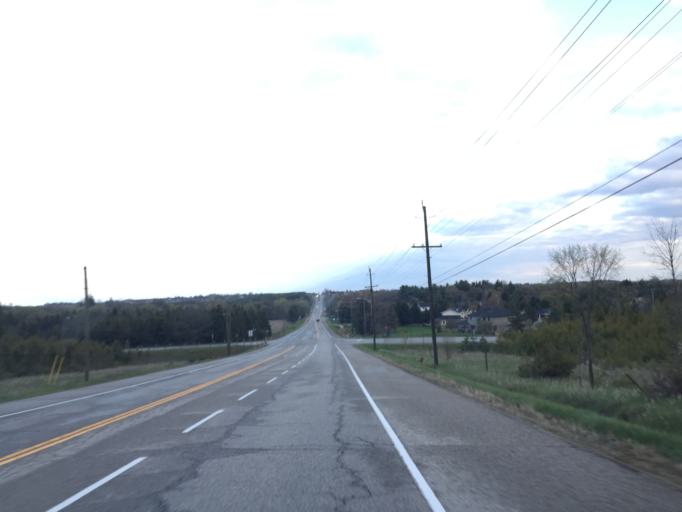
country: CA
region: Ontario
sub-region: Wellington County
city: Guelph
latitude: 43.5916
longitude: -80.2791
